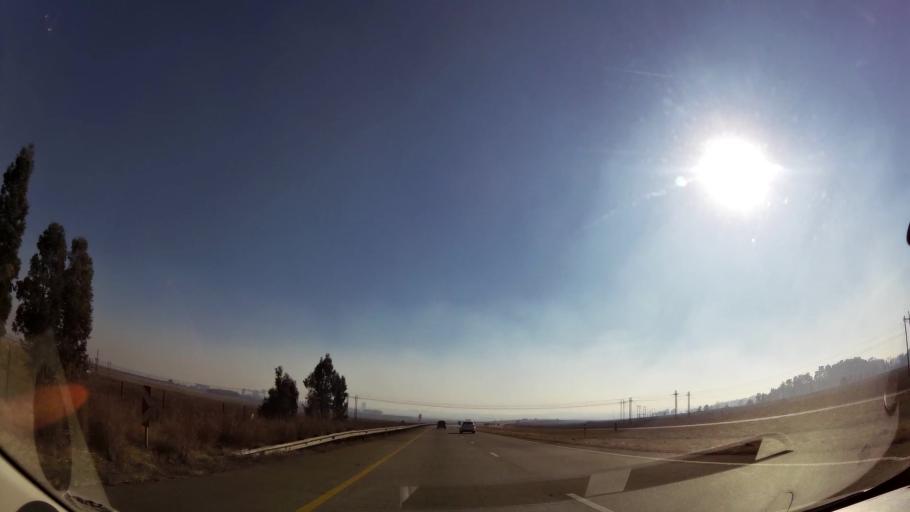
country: ZA
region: Mpumalanga
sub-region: Nkangala District Municipality
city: Witbank
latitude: -25.9532
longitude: 29.1968
